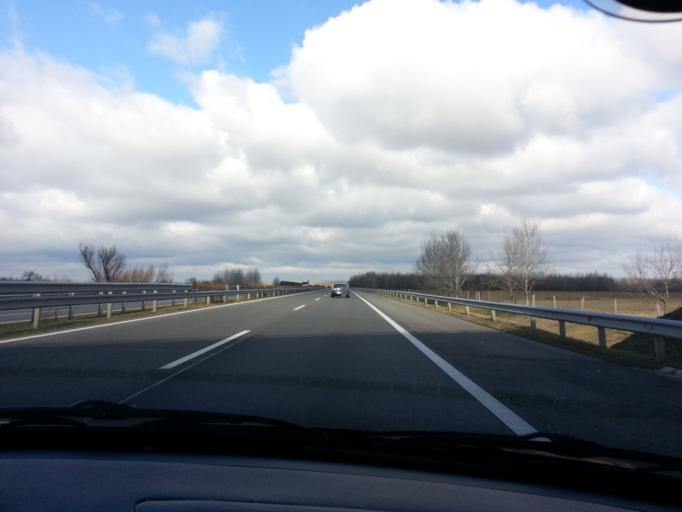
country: HU
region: Csongrad
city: Csengele
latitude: 46.5009
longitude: 19.9131
